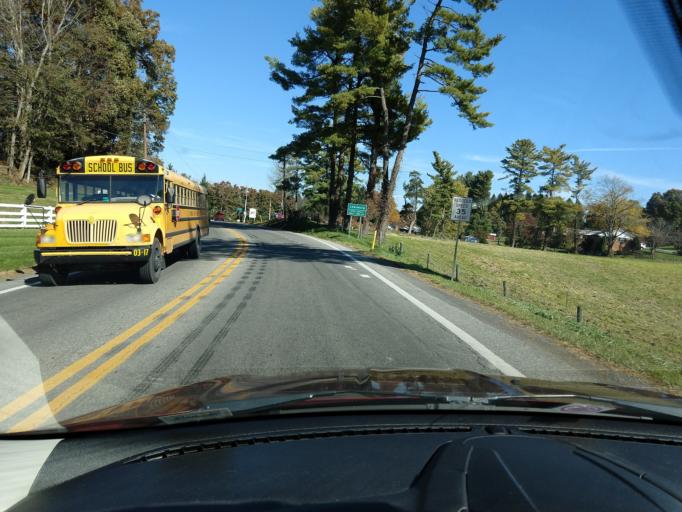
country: US
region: West Virginia
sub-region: Greenbrier County
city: Lewisburg
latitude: 37.7914
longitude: -80.4464
